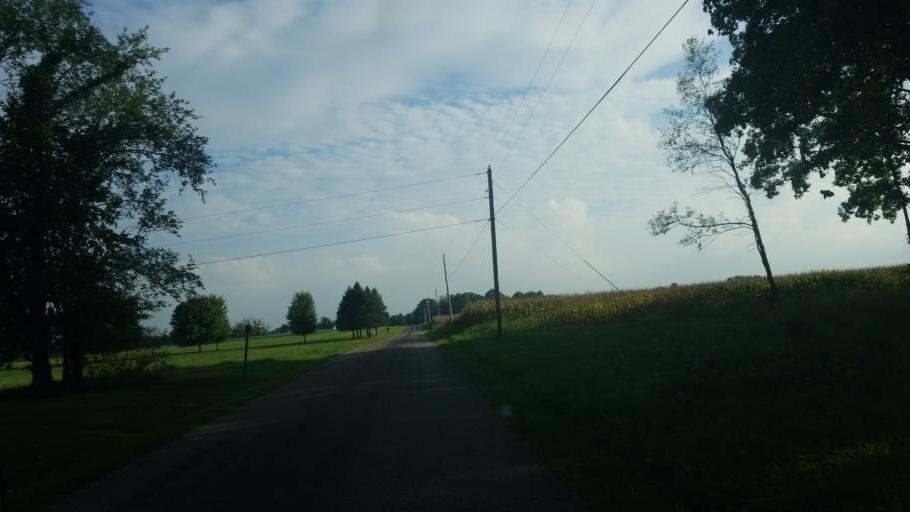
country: US
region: Ohio
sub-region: Wayne County
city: West Salem
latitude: 40.9064
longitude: -82.0225
